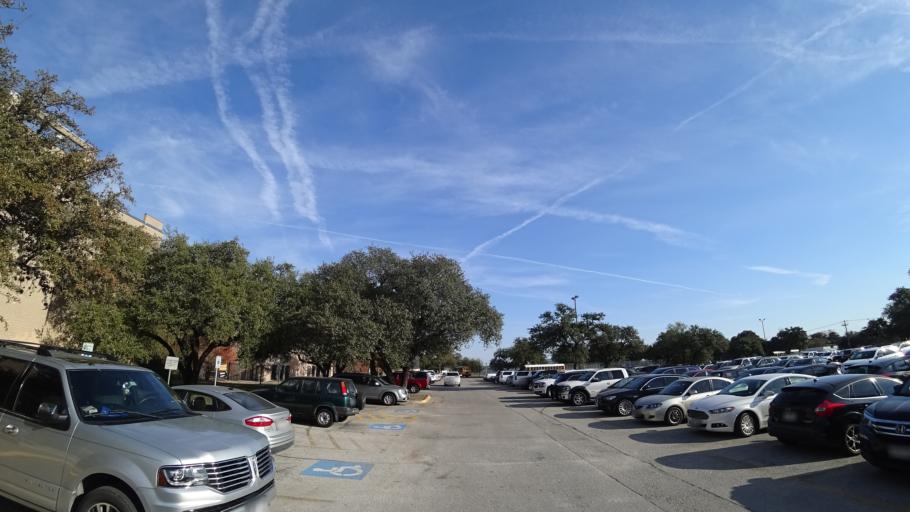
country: US
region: Texas
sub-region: Williamson County
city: Jollyville
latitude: 30.3751
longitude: -97.7540
